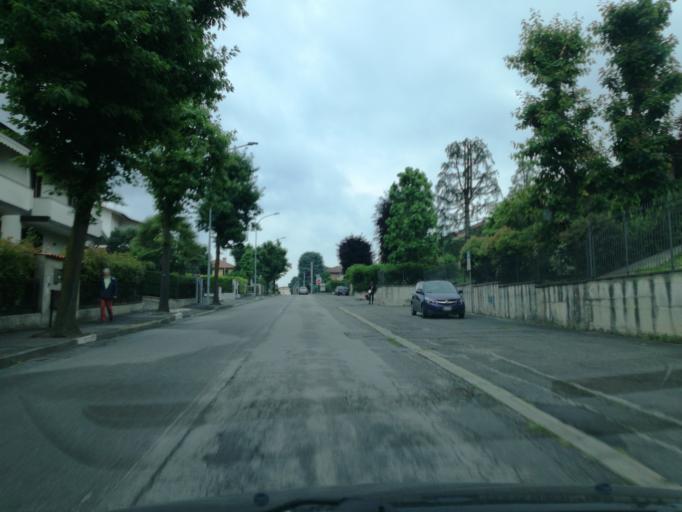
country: IT
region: Lombardy
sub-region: Provincia di Monza e Brianza
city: Carnate
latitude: 45.6492
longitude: 9.3752
